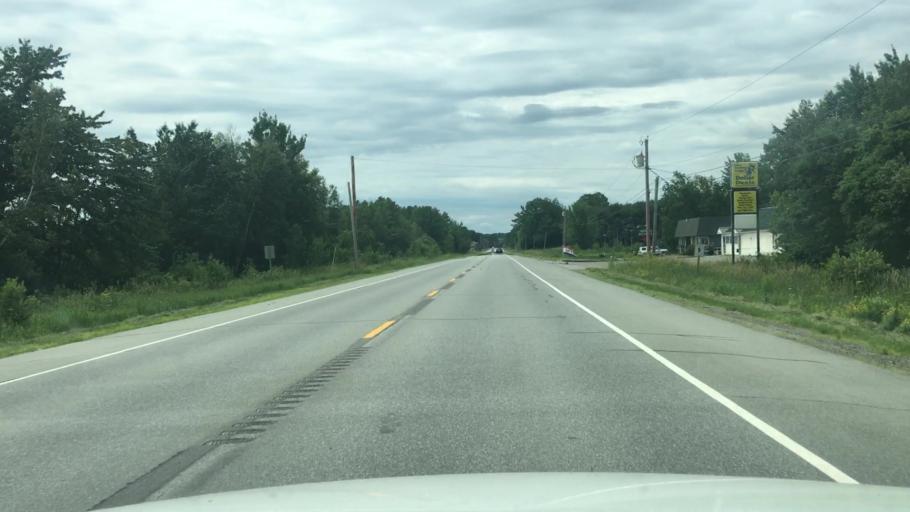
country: US
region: Maine
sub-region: Kennebec County
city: Windsor
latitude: 44.3909
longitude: -69.5832
